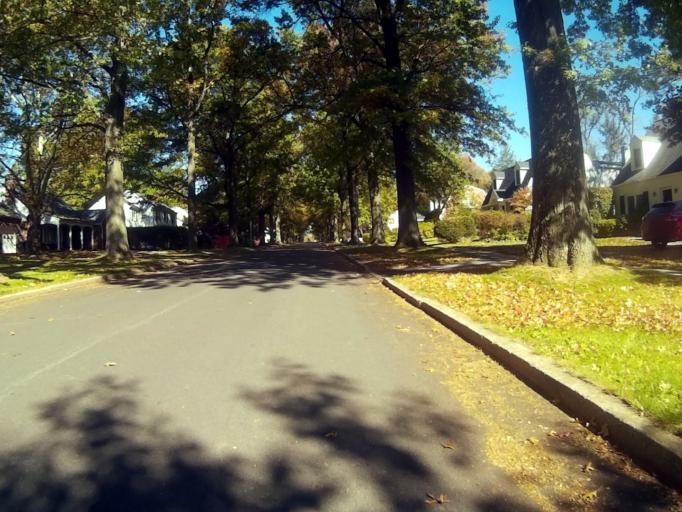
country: US
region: Pennsylvania
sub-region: Centre County
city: State College
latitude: 40.7933
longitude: -77.8769
